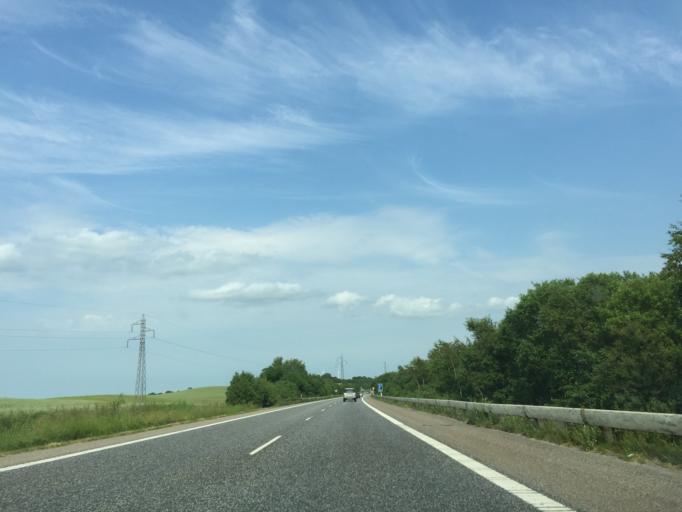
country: DK
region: Central Jutland
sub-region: Syddjurs Kommune
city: Hornslet
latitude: 56.3066
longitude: 10.3589
